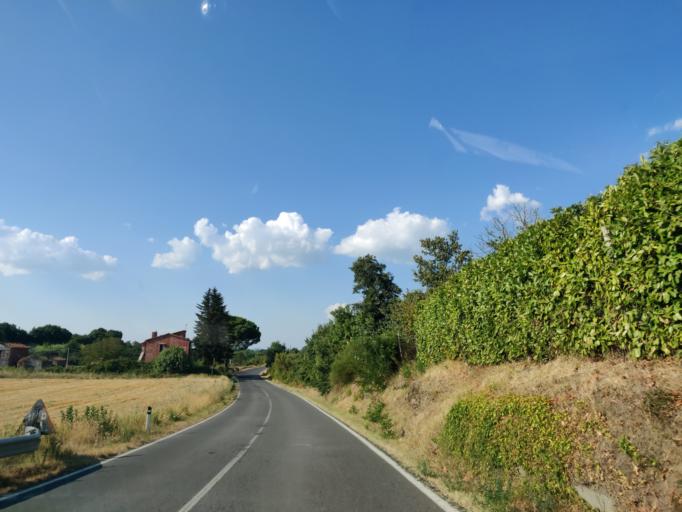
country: IT
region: Latium
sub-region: Provincia di Viterbo
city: Gradoli
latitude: 42.6609
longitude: 11.8522
